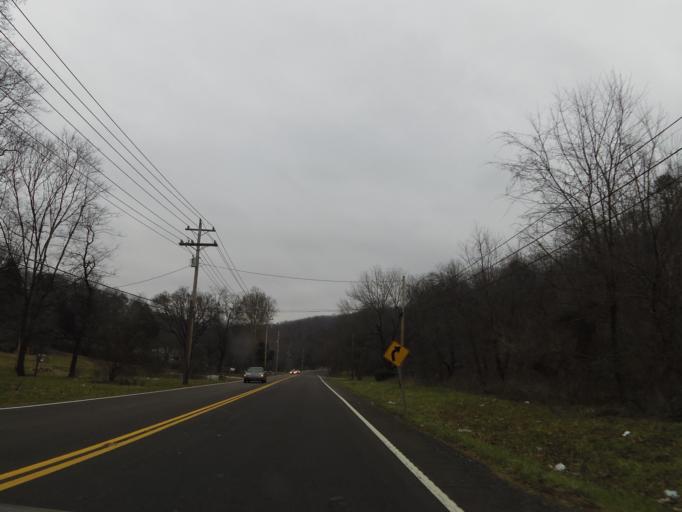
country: US
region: Tennessee
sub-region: Anderson County
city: Clinton
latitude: 36.1235
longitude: -84.1396
